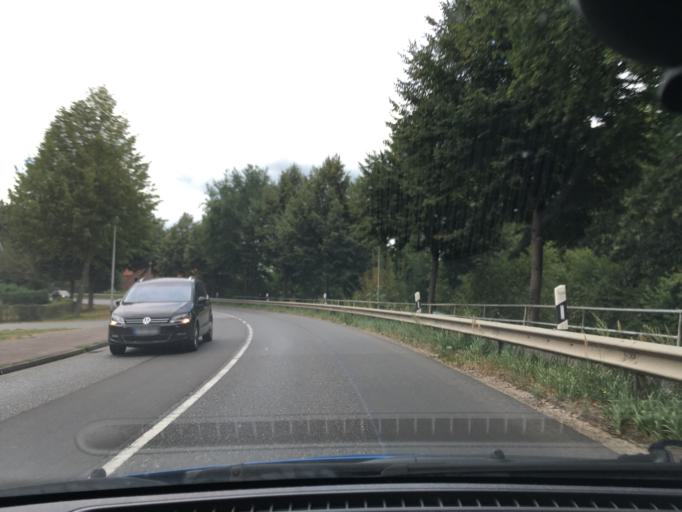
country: DE
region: Lower Saxony
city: Neu Wulmstorf
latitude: 53.4482
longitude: 9.7571
